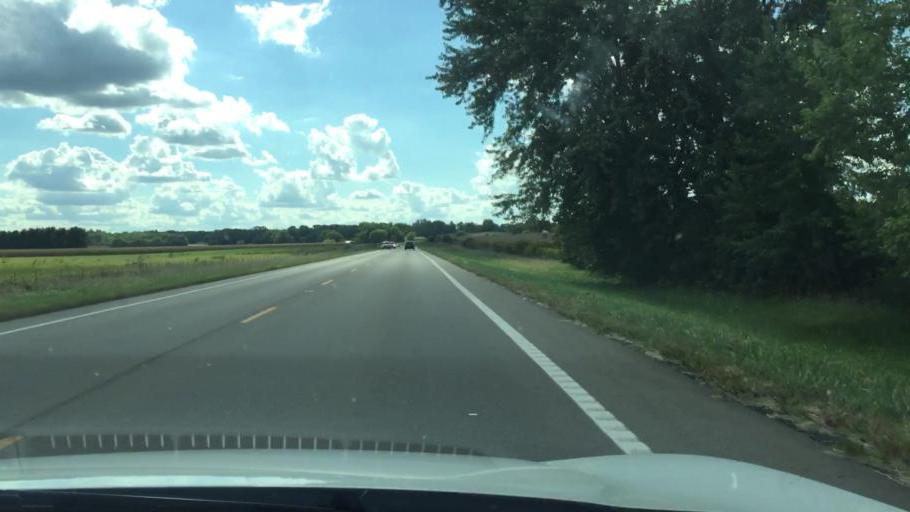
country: US
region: Ohio
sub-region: Clark County
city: Northridge
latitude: 40.0050
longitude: -83.7150
